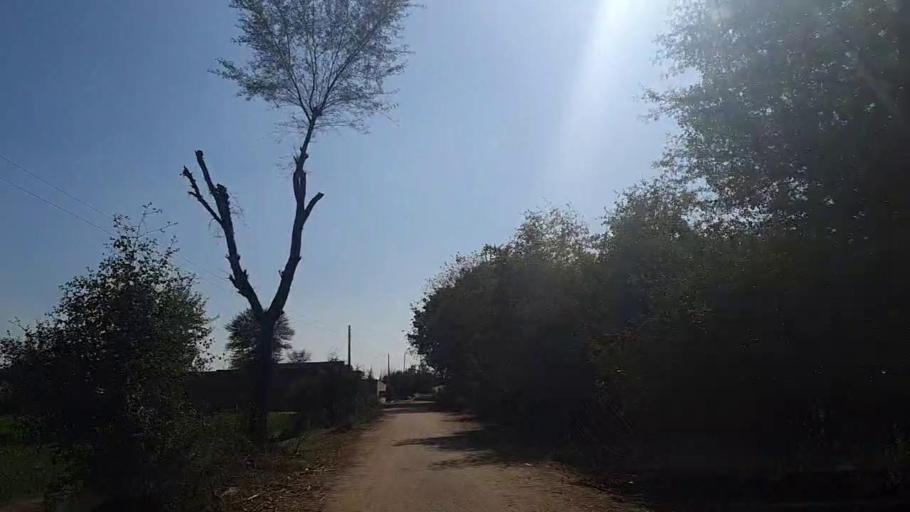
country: PK
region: Sindh
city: Sakrand
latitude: 26.2323
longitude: 68.1998
